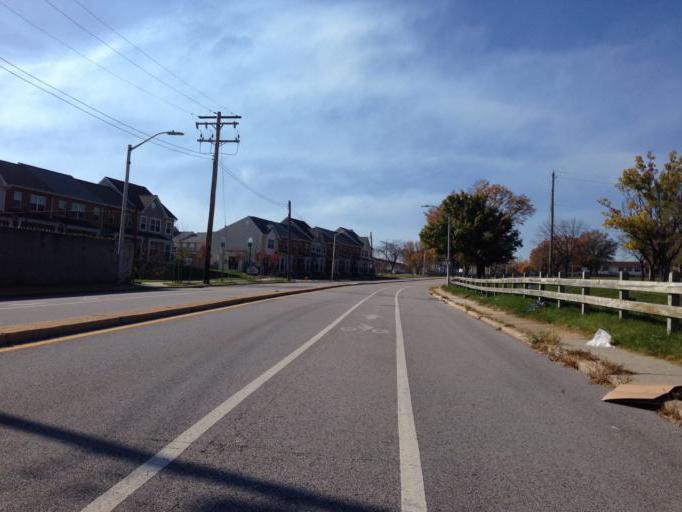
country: US
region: Maryland
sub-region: Baltimore County
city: Dundalk
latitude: 39.2785
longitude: -76.5377
